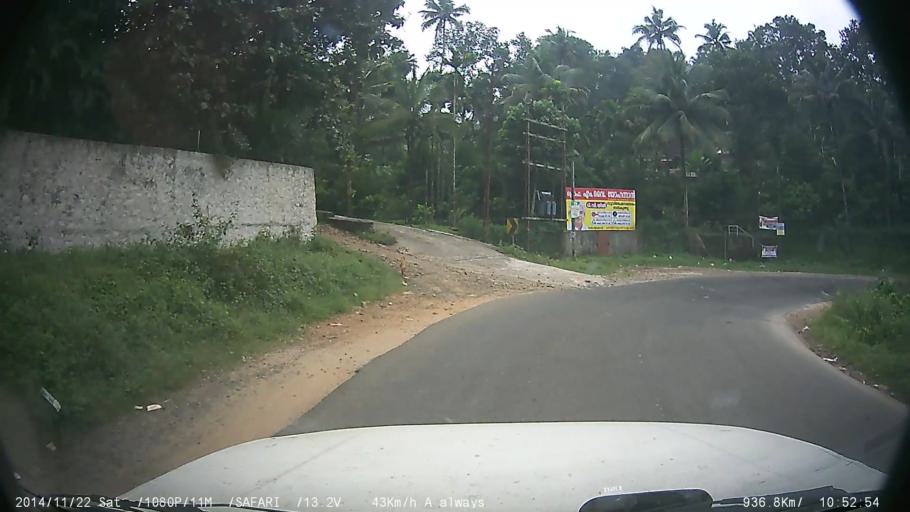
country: IN
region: Kerala
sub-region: Ernakulam
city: Muvattupuzha
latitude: 9.9631
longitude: 76.5792
